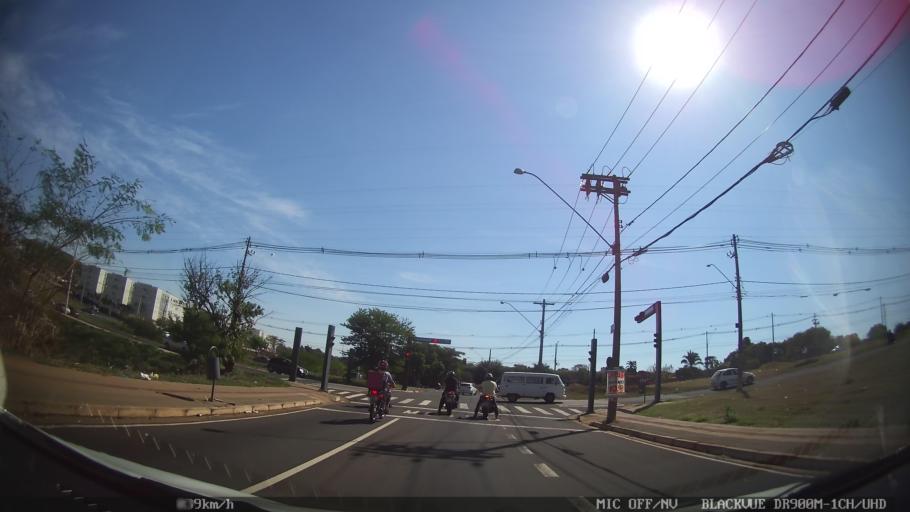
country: BR
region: Sao Paulo
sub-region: Sao Jose Do Rio Preto
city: Sao Jose do Rio Preto
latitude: -20.7754
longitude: -49.3969
